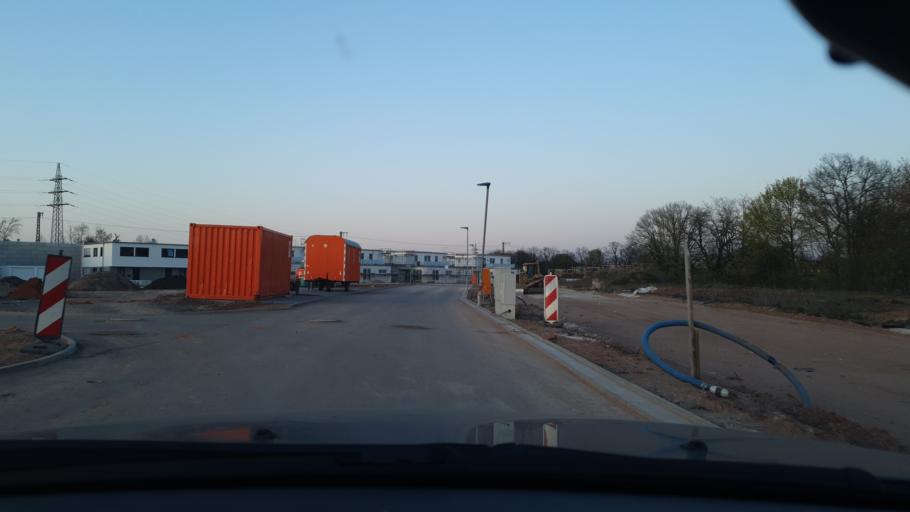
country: DE
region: Rheinland-Pfalz
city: Kaiserslautern
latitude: 49.4401
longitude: 7.7288
